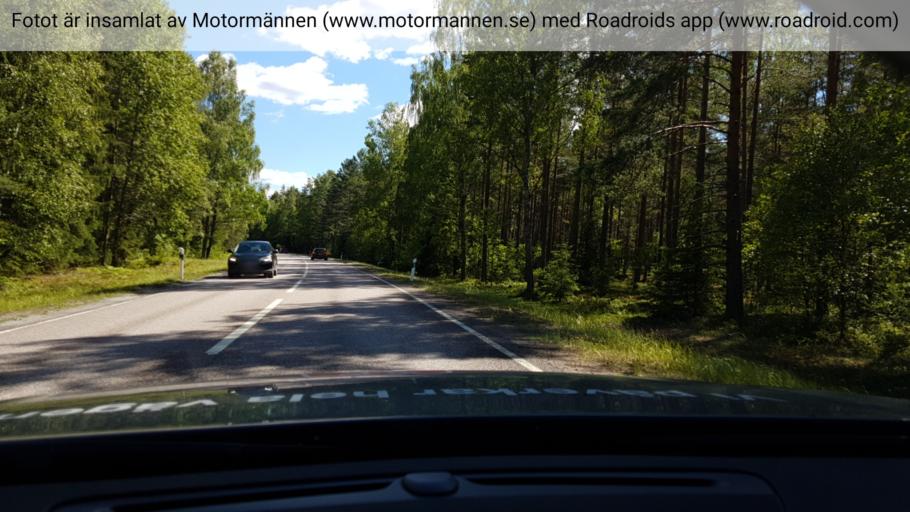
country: SE
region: Soedermanland
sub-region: Flens Kommun
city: Malmkoping
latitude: 59.1945
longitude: 16.7891
